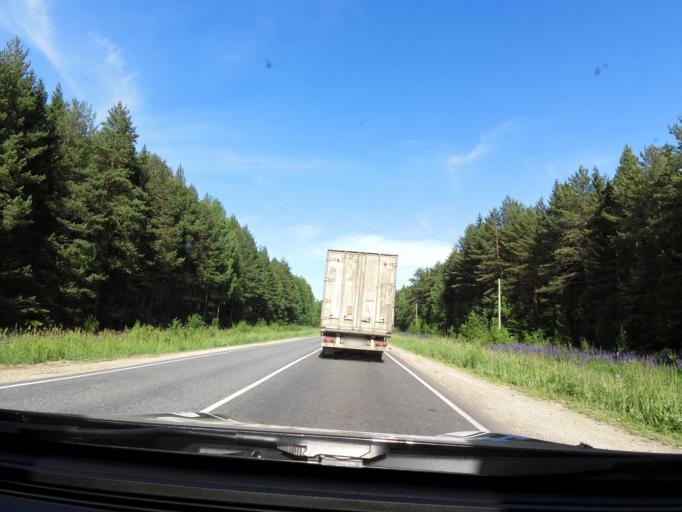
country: RU
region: Kirov
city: Belaya Kholunitsa
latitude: 58.8729
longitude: 50.8530
